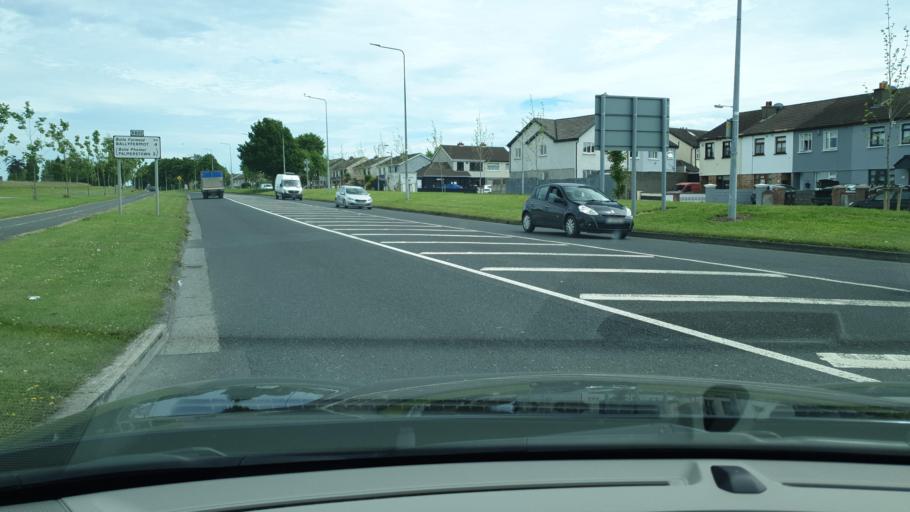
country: IE
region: Leinster
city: Clondalkin
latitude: 53.3485
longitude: -6.4046
